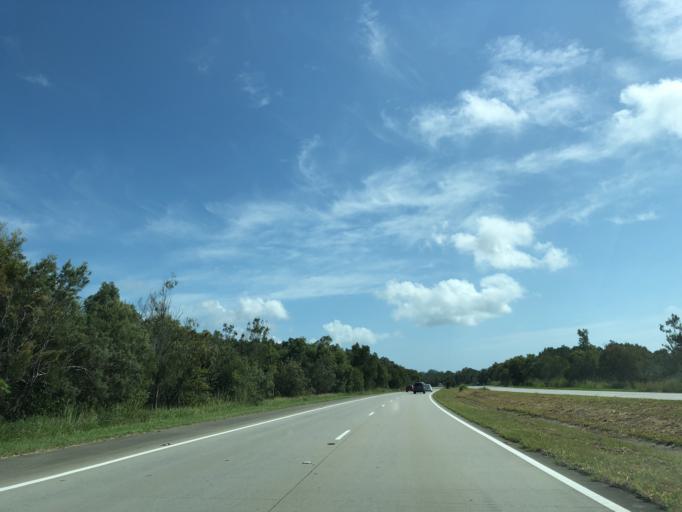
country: AU
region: New South Wales
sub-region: Byron Shire
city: Brunswick Heads
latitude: -28.5680
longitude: 153.5408
